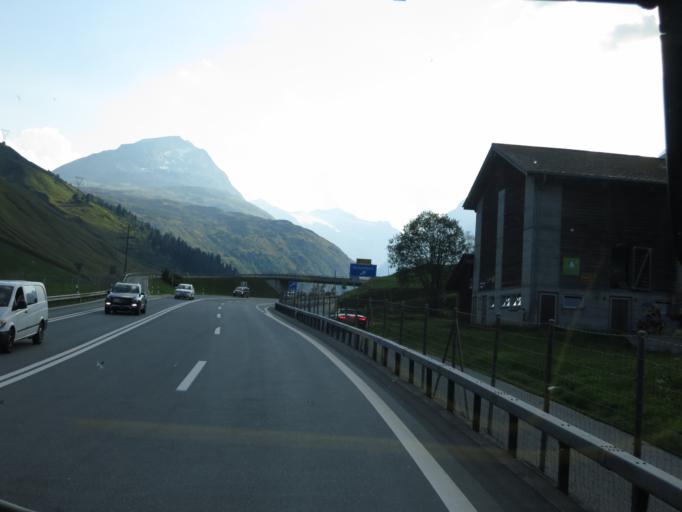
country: CH
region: Grisons
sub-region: Hinterrhein District
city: Hinterrhein
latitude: 46.5316
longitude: 9.2059
